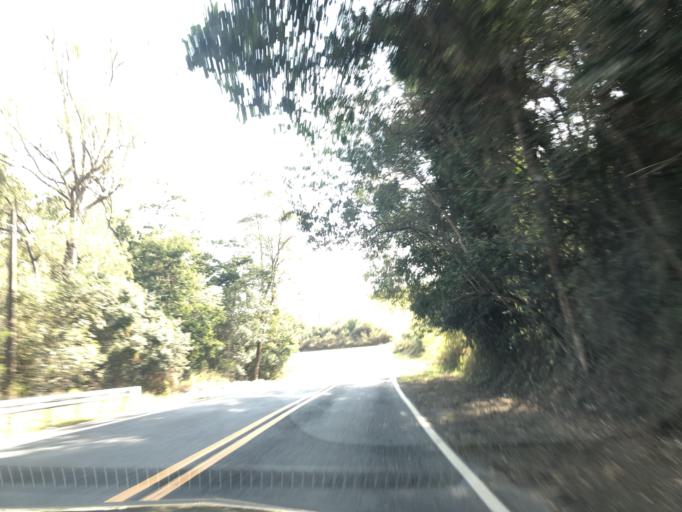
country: BR
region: Sao Paulo
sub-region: Pilar Do Sul
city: Pilar do Sul
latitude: -23.8179
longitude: -47.6521
